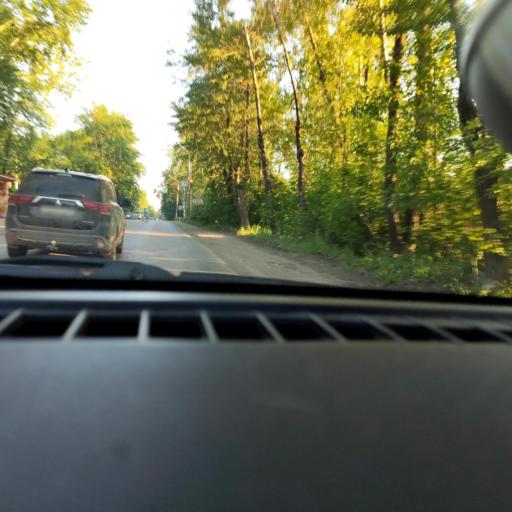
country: RU
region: Perm
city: Polazna
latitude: 58.1283
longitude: 56.3729
